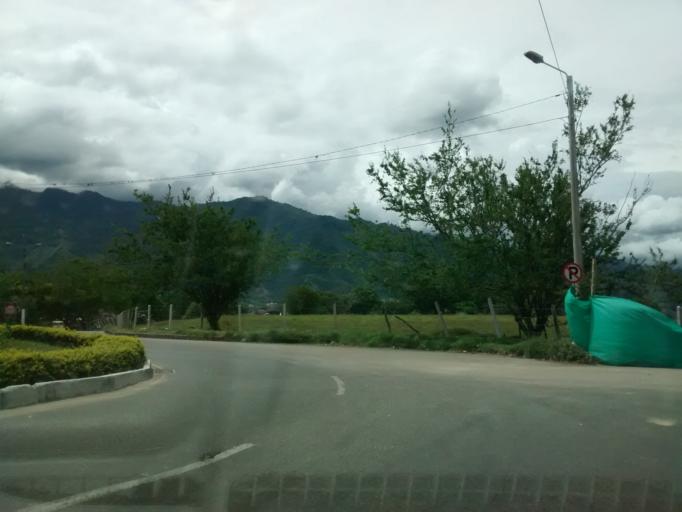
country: CO
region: Tolima
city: Ibague
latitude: 4.4306
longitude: -75.1995
